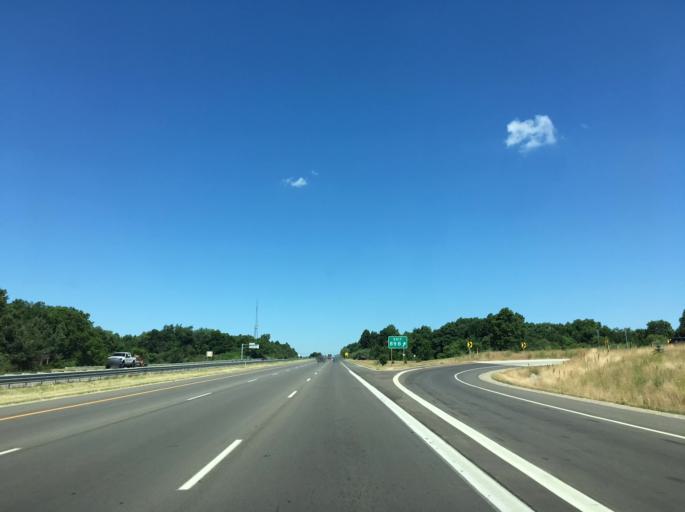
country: US
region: Michigan
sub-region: Oakland County
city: Clarkston
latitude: 42.7367
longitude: -83.3806
